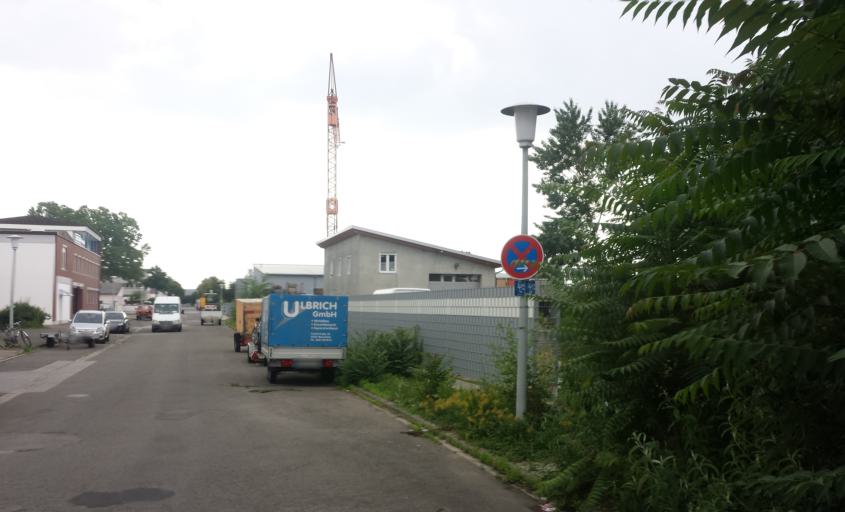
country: DE
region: Rheinland-Pfalz
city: Altrip
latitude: 49.4636
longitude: 8.4990
